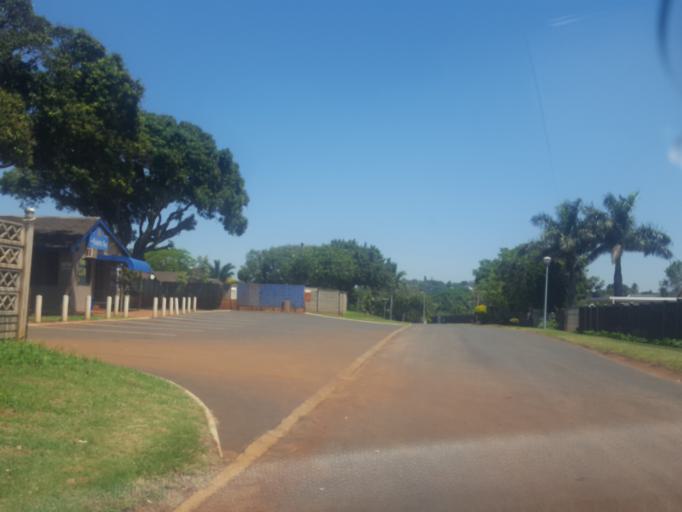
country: ZA
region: KwaZulu-Natal
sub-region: uThungulu District Municipality
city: Empangeni
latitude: -28.7479
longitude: 31.9069
